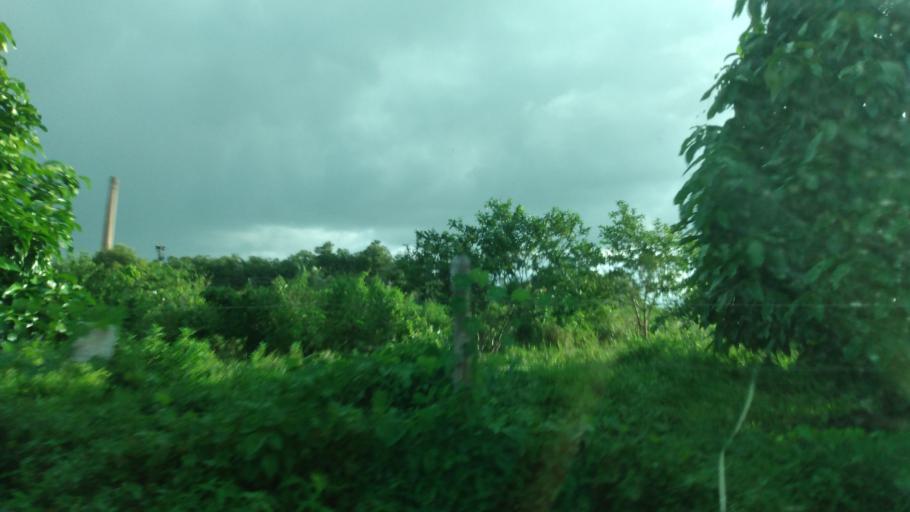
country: BR
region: Pernambuco
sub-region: Palmares
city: Palmares
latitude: -8.6797
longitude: -35.5964
